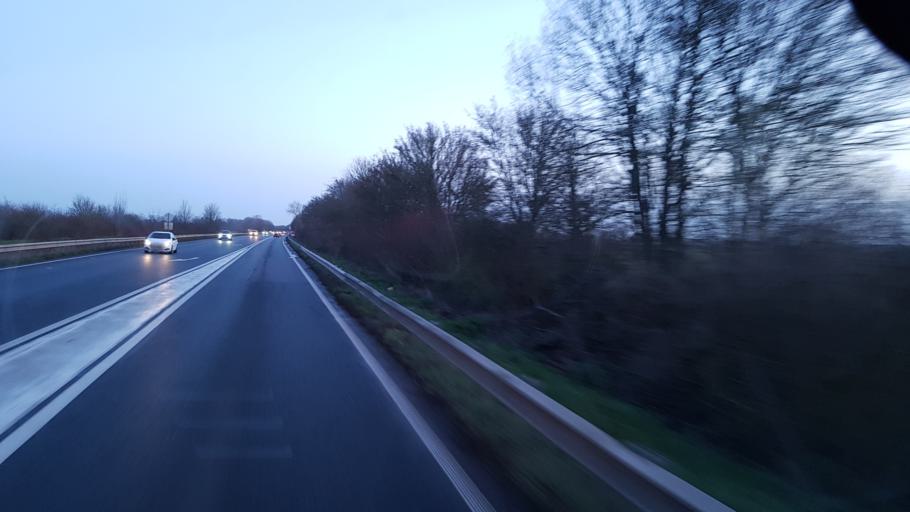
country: FR
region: Nord-Pas-de-Calais
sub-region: Departement du Nord
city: Lambres-lez-Douai
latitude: 50.3422
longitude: 3.0787
